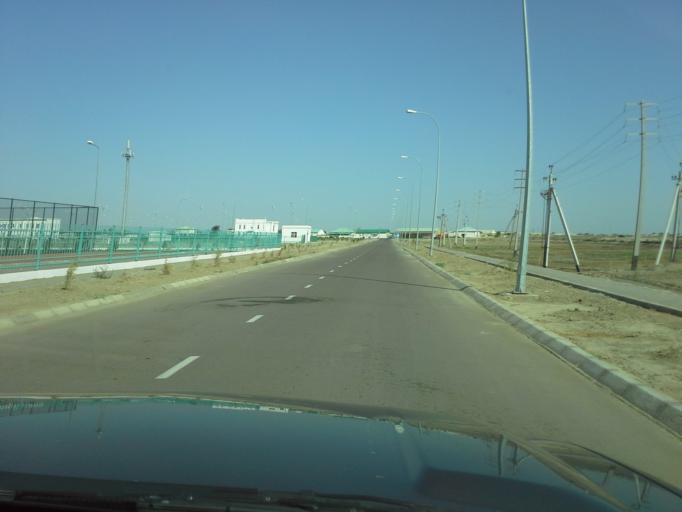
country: TM
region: Dasoguz
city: Dasoguz
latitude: 41.8126
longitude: 59.9534
